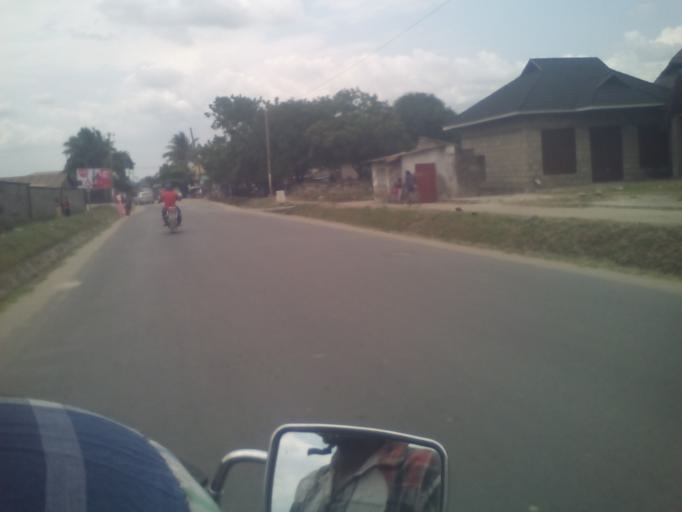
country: TZ
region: Dar es Salaam
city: Dar es Salaam
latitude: -6.8622
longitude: 39.2213
